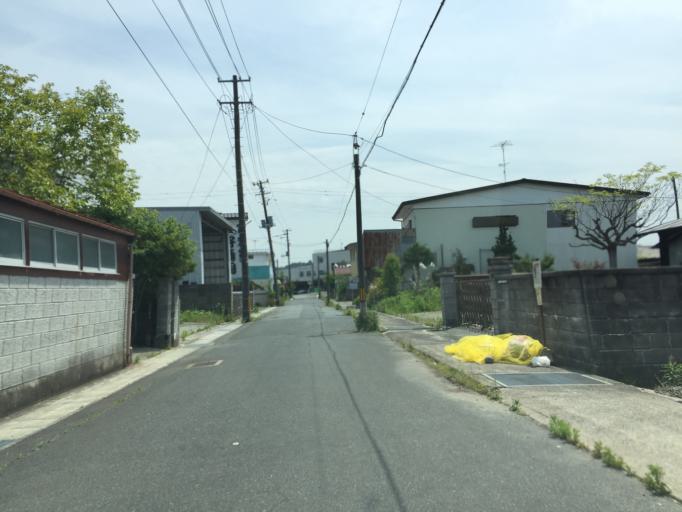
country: JP
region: Fukushima
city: Namie
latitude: 37.4912
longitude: 140.9939
